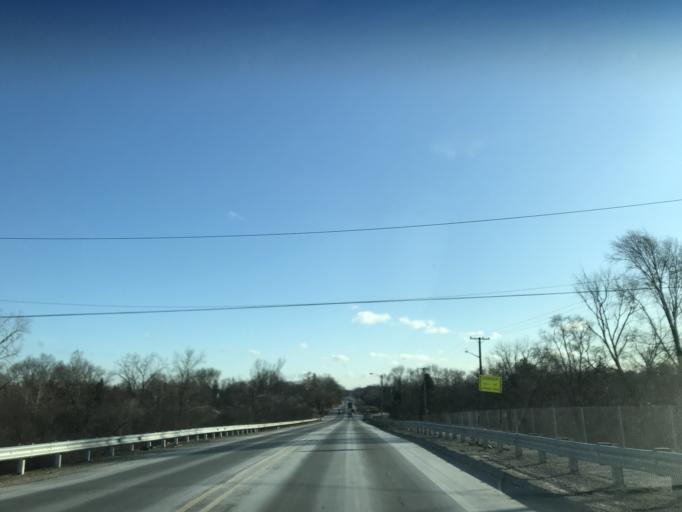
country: US
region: Michigan
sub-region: Oakland County
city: Troy
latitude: 42.5772
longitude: -83.1585
